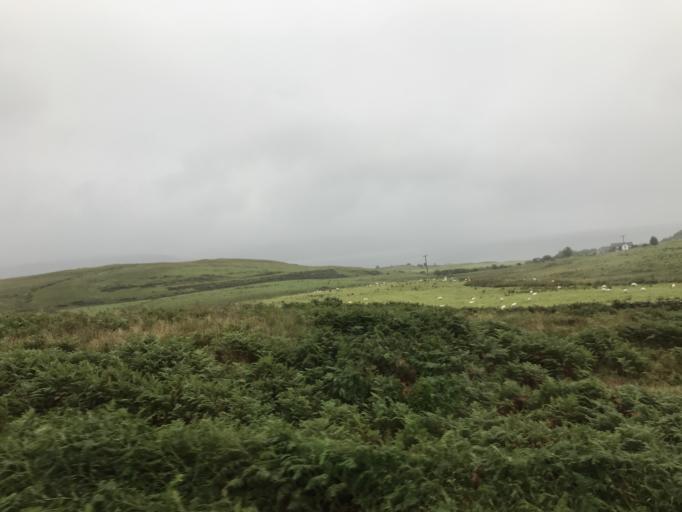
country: GB
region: Scotland
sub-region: Argyll and Bute
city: Isle Of Mull
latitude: 56.5740
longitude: -6.0019
